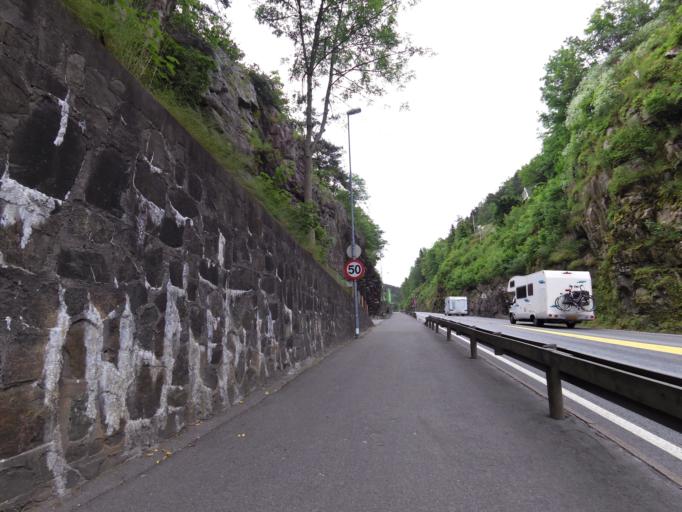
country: NO
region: Vest-Agder
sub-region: Flekkefjord
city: Flekkefjord
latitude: 58.2965
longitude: 6.6707
